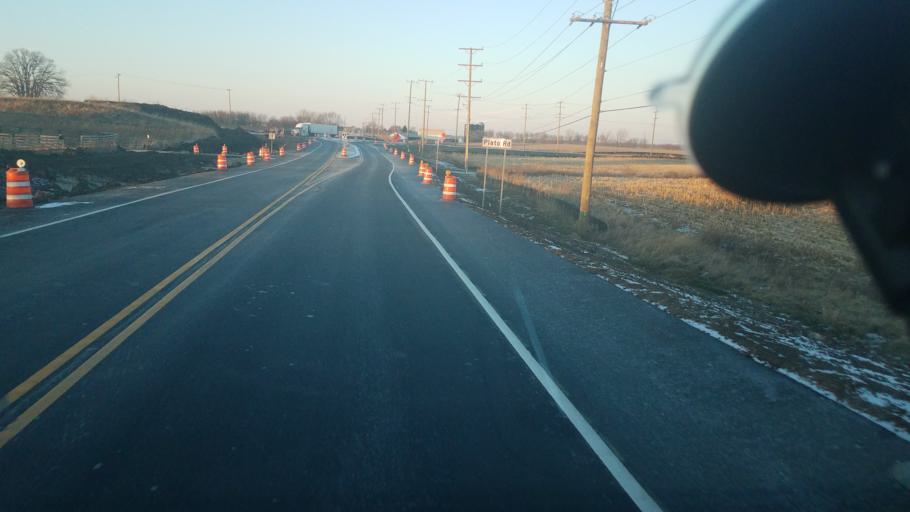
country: US
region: Illinois
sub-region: Kane County
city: Pingree Grove
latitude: 42.0174
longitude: -88.4640
